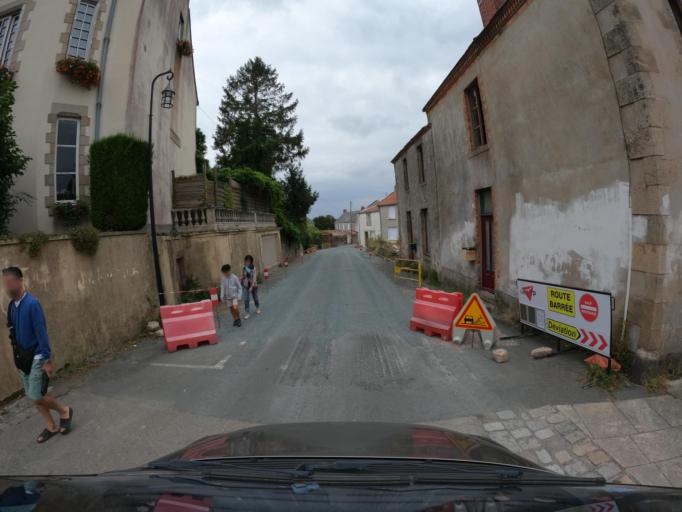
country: FR
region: Pays de la Loire
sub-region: Departement de la Vendee
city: Tiffauges
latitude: 47.0137
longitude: -1.1141
